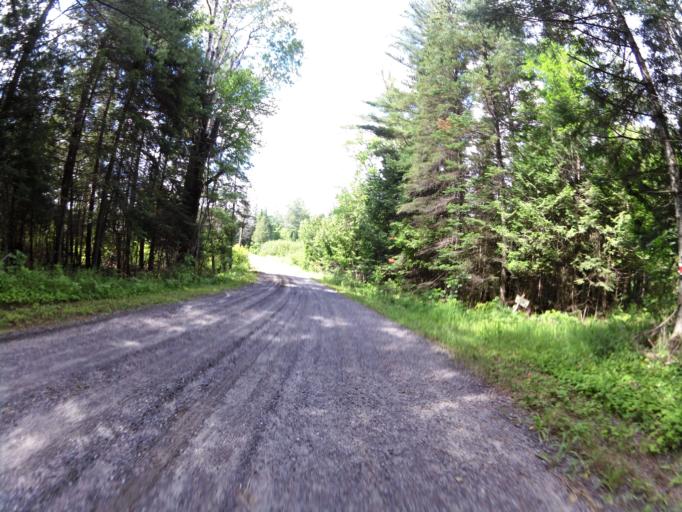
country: CA
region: Ontario
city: Perth
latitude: 45.0740
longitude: -76.4697
